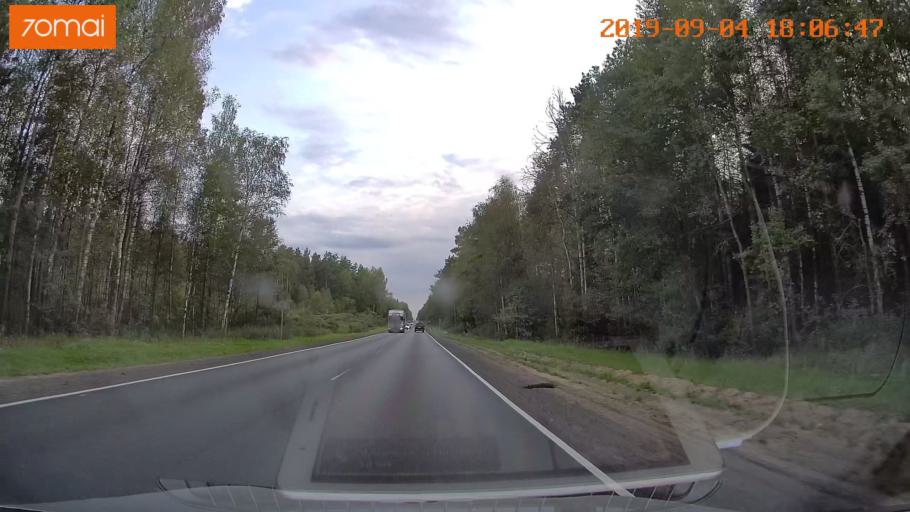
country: RU
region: Moskovskaya
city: Khorlovo
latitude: 55.4273
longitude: 38.8103
